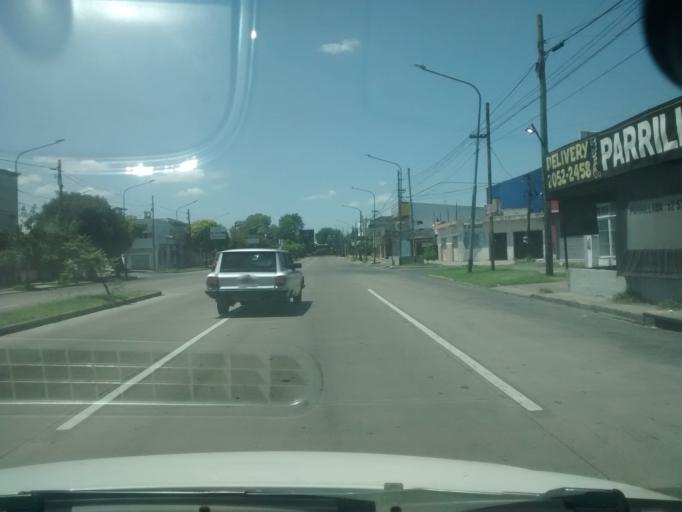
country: AR
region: Buenos Aires
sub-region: Partido de Moron
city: Moron
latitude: -34.6604
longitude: -58.6104
